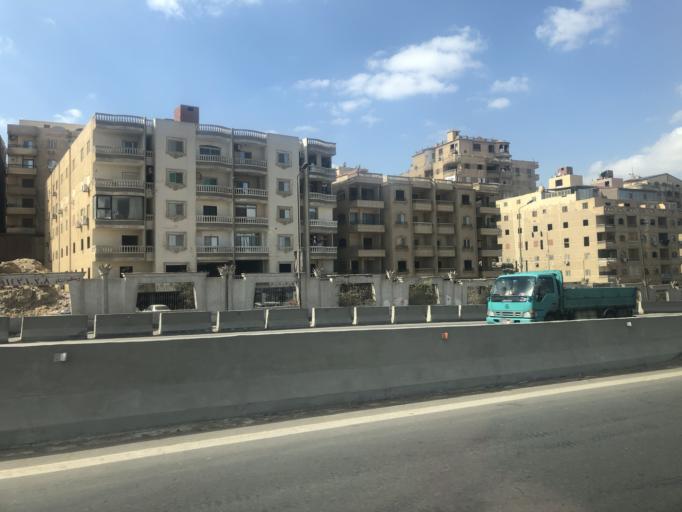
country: EG
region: Al Jizah
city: Al Jizah
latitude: 29.9671
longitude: 31.1087
